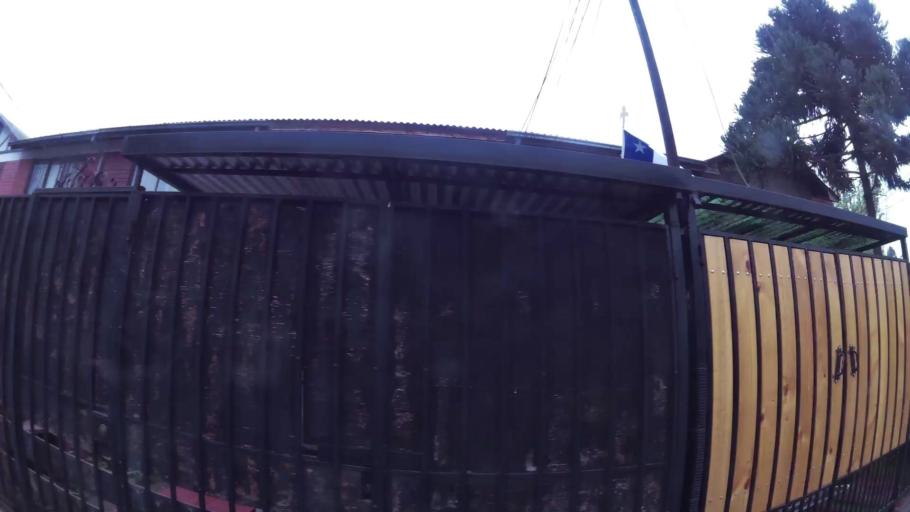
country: CL
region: Santiago Metropolitan
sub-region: Provincia de Santiago
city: Villa Presidente Frei, Nunoa, Santiago, Chile
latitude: -33.5031
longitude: -70.6011
